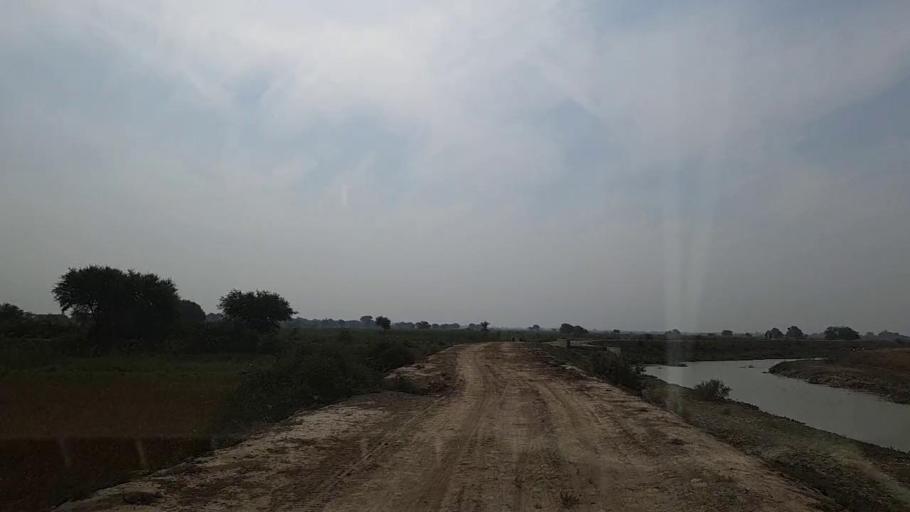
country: PK
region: Sindh
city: Mirpur Batoro
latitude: 24.6625
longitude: 68.2506
